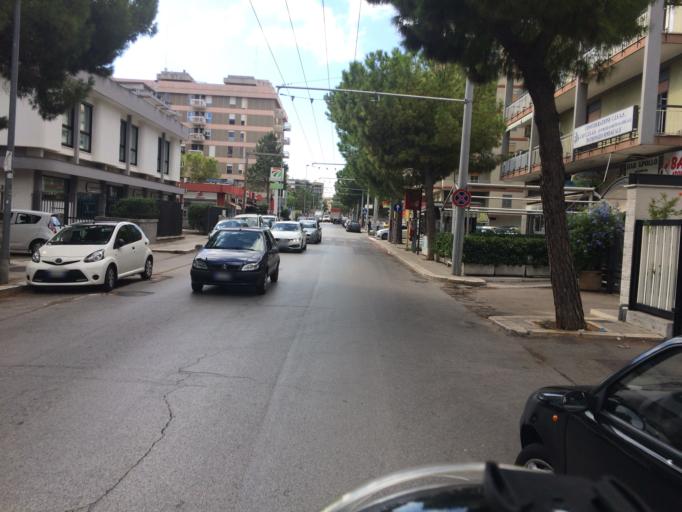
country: IT
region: Apulia
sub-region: Provincia di Bari
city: Bari
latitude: 41.0986
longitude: 16.8711
